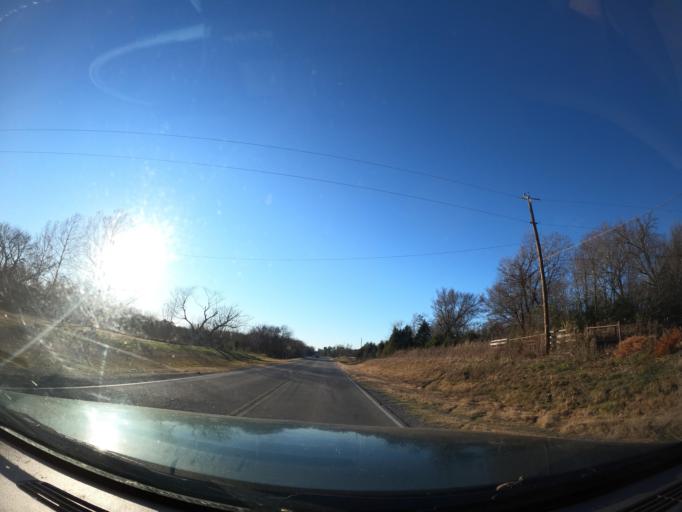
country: US
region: Oklahoma
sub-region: Pittsburg County
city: Hartshorne
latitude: 34.8876
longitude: -95.4744
